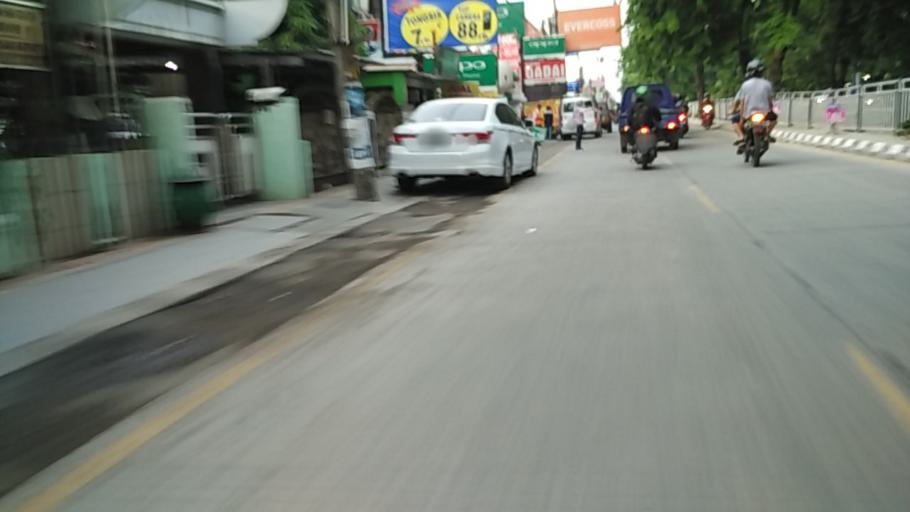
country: ID
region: Central Java
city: Semarang
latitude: -6.9845
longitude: 110.4593
